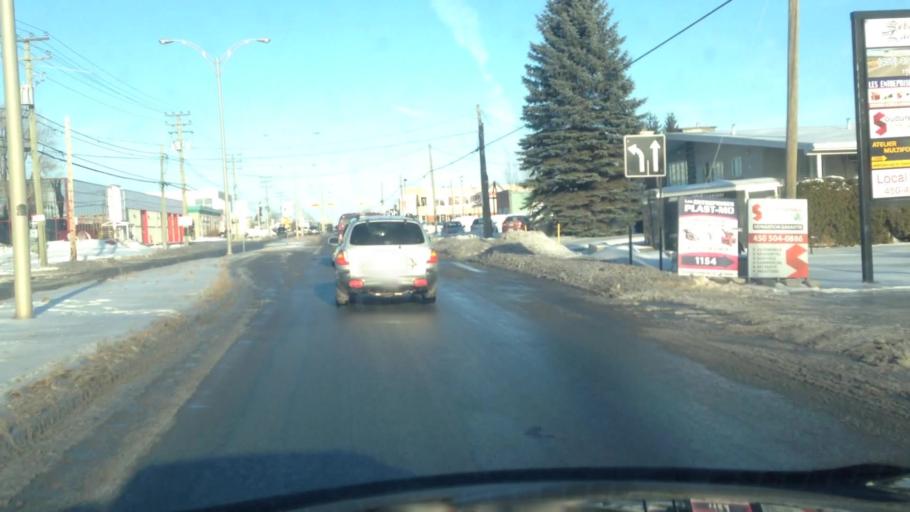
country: CA
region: Quebec
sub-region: Laurentides
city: Saint-Jerome
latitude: 45.7669
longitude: -73.9777
